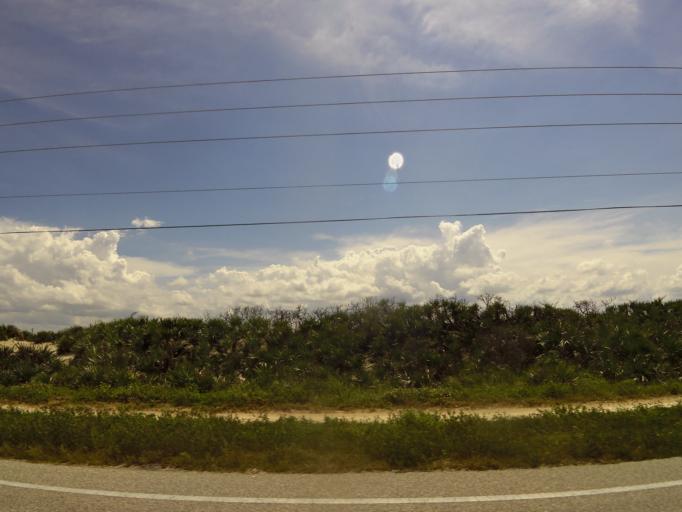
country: US
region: Florida
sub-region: Volusia County
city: Ormond-by-the-Sea
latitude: 29.4120
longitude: -81.0956
